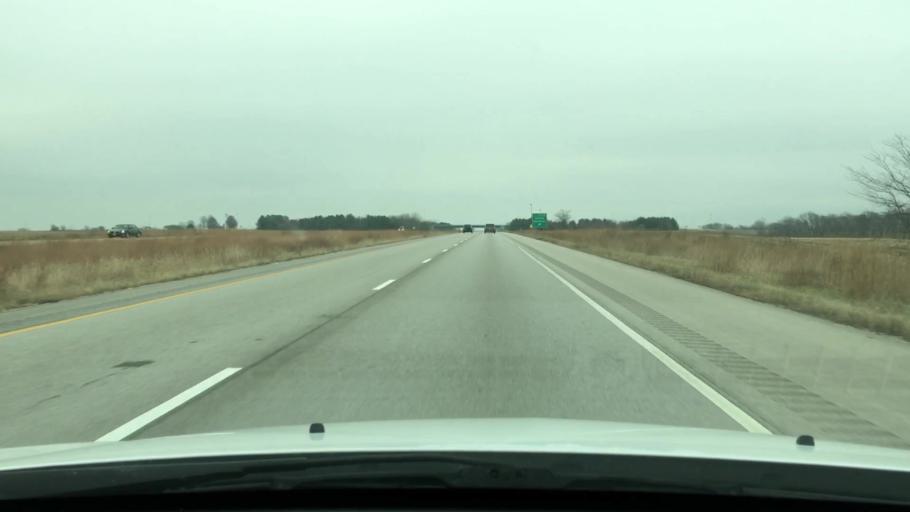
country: US
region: Illinois
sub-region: Sangamon County
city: New Berlin
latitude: 39.7368
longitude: -90.0518
